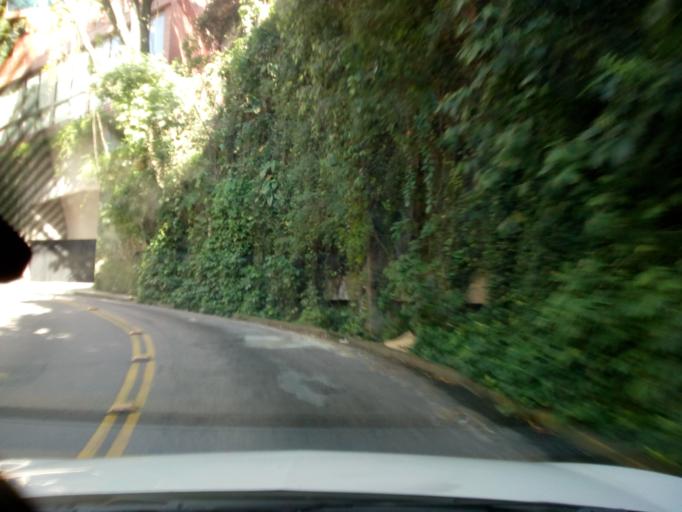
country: BR
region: Rio de Janeiro
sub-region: Rio De Janeiro
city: Rio de Janeiro
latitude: -22.9830
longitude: -43.2322
